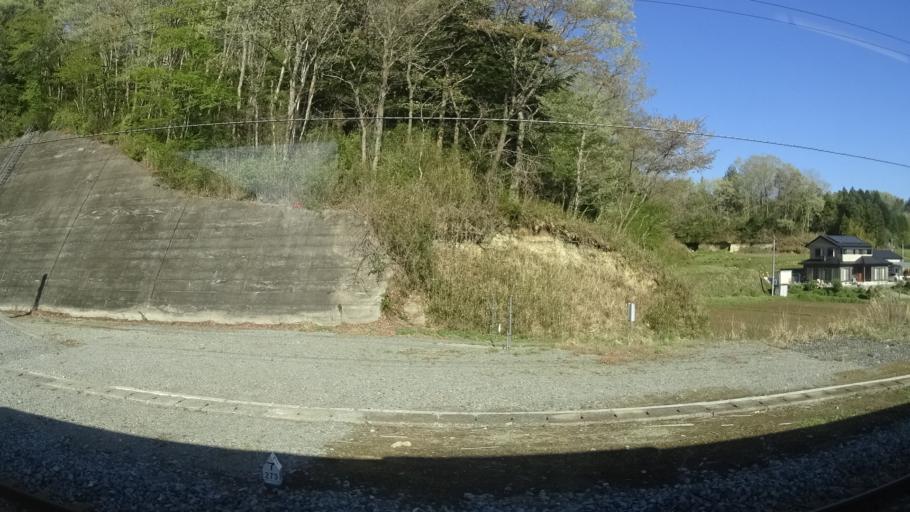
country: JP
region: Fukushima
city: Namie
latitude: 37.5305
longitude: 140.9852
